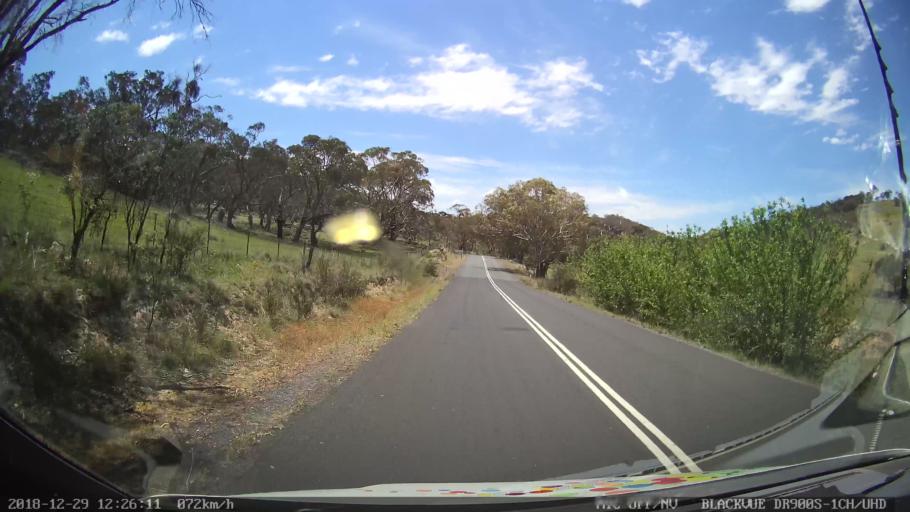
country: AU
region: New South Wales
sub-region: Queanbeyan
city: Queanbeyan
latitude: -35.4633
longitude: 149.2214
